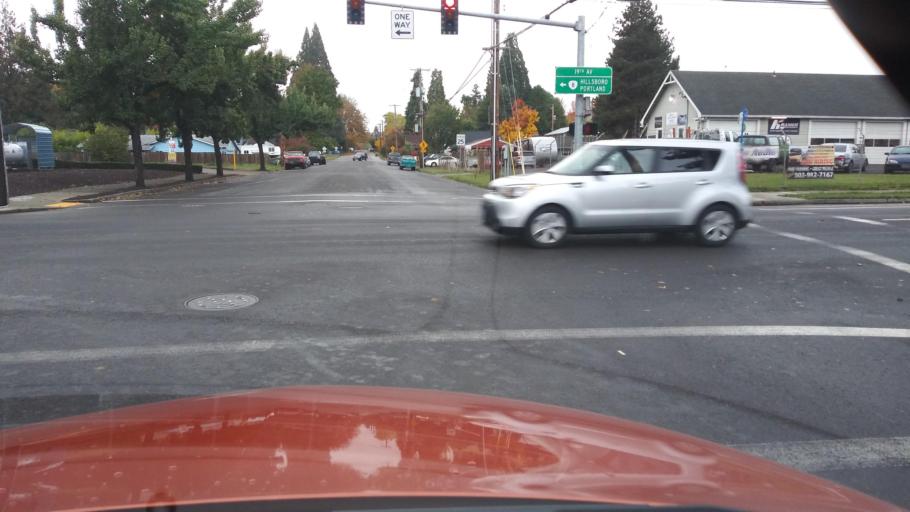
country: US
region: Oregon
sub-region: Washington County
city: Forest Grove
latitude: 45.5185
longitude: -123.0993
